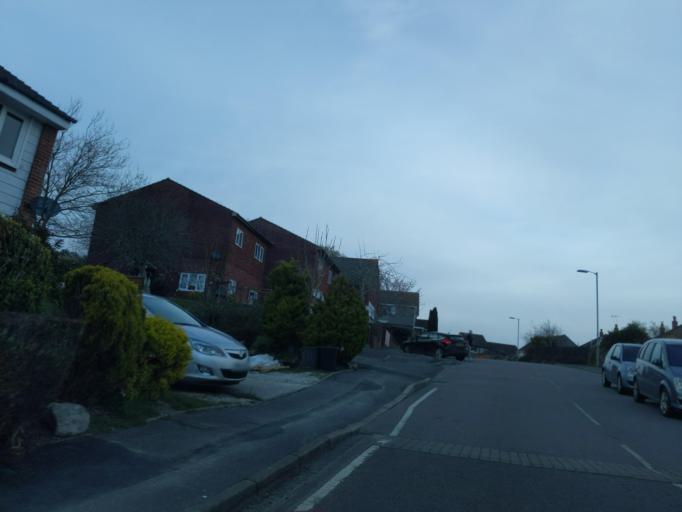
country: GB
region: England
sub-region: Cornwall
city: Torpoint
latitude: 50.3767
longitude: -4.2134
